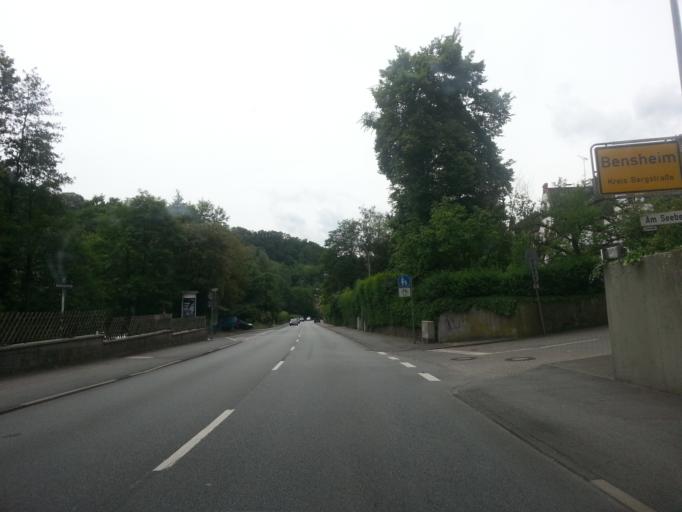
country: DE
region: Hesse
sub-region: Regierungsbezirk Darmstadt
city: Bensheim
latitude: 49.6891
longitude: 8.6449
